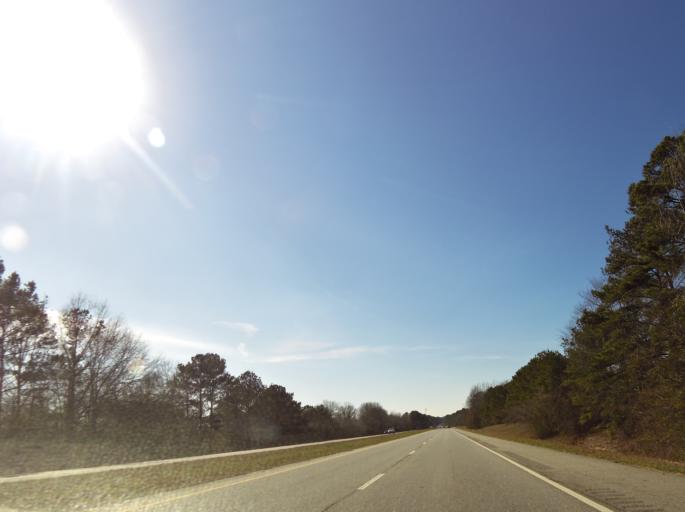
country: US
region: Georgia
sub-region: Bibb County
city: West Point
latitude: 32.8003
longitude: -83.7474
